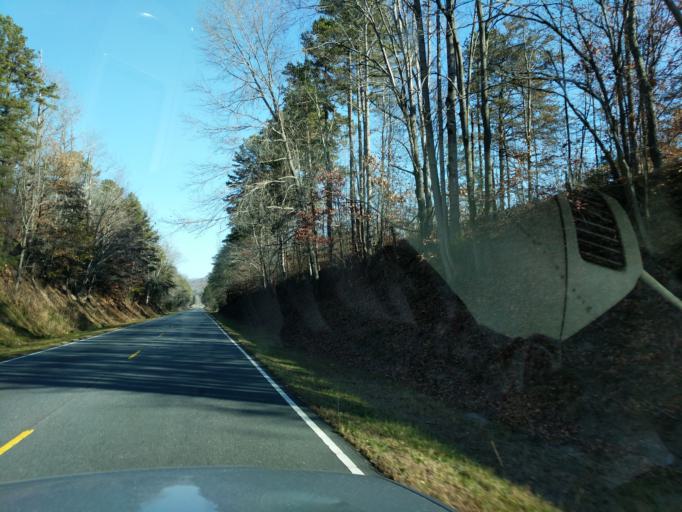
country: US
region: North Carolina
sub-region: Rutherford County
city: Rutherfordton
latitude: 35.5016
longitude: -81.9769
